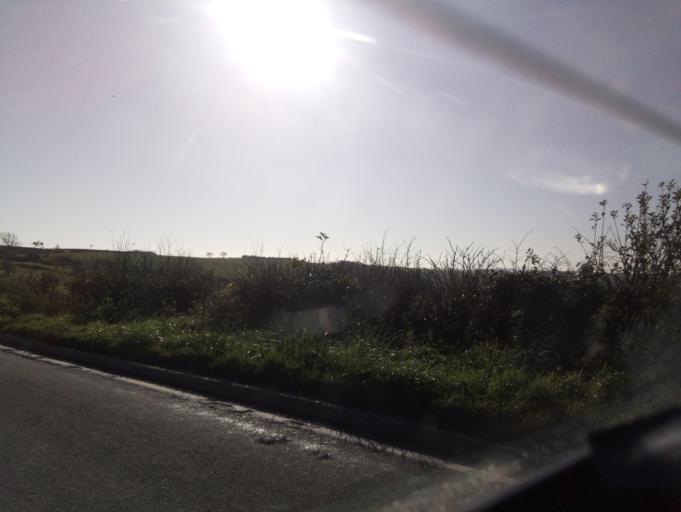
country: GB
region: England
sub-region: Dorset
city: Dorchester
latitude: 50.8200
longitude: -2.4577
